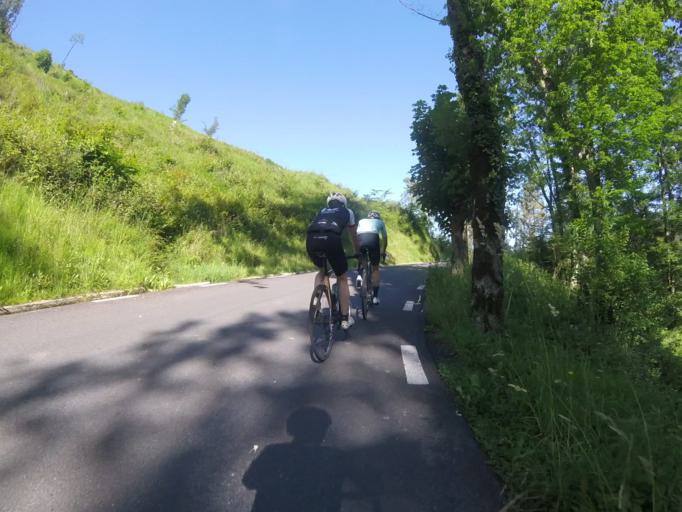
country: ES
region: Basque Country
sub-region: Provincia de Guipuzcoa
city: Beizama
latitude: 43.1390
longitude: -2.2200
